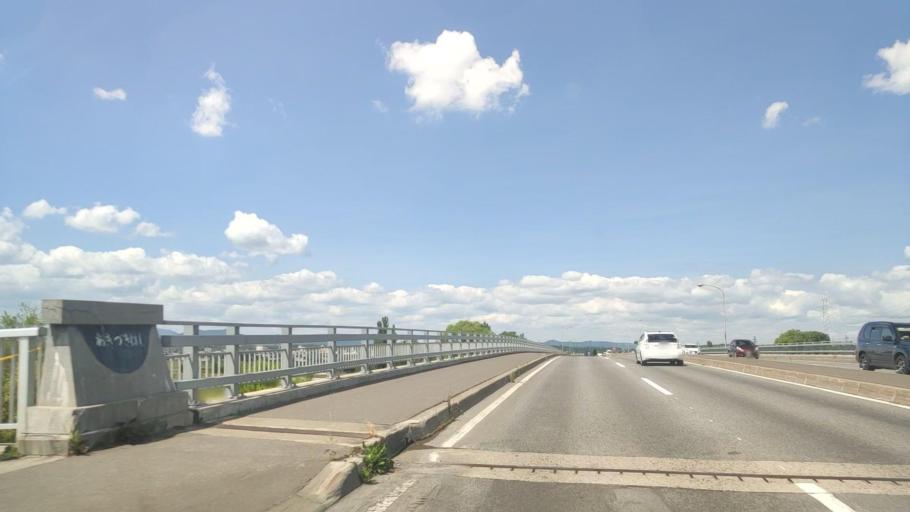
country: JP
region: Hokkaido
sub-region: Asahikawa-shi
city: Asahikawa
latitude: 43.7966
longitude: 142.3975
